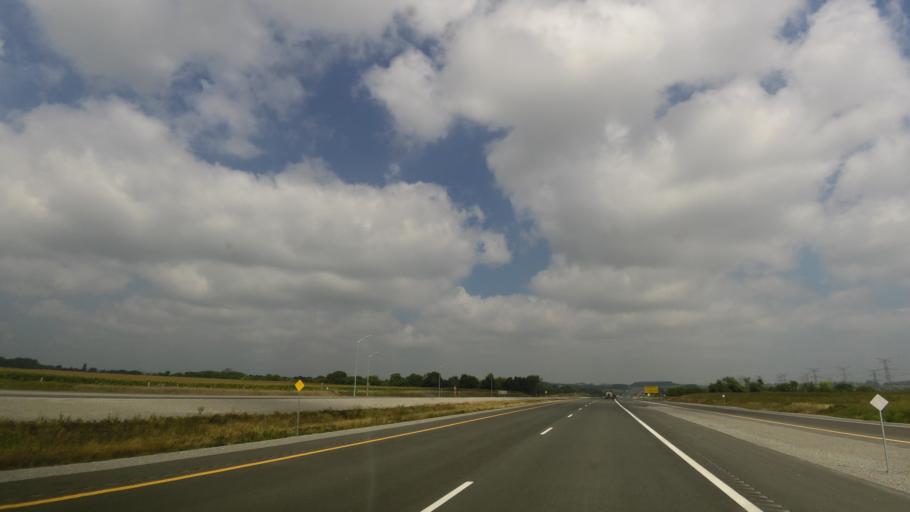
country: CA
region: Ontario
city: Oshawa
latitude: 43.9724
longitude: -78.9016
